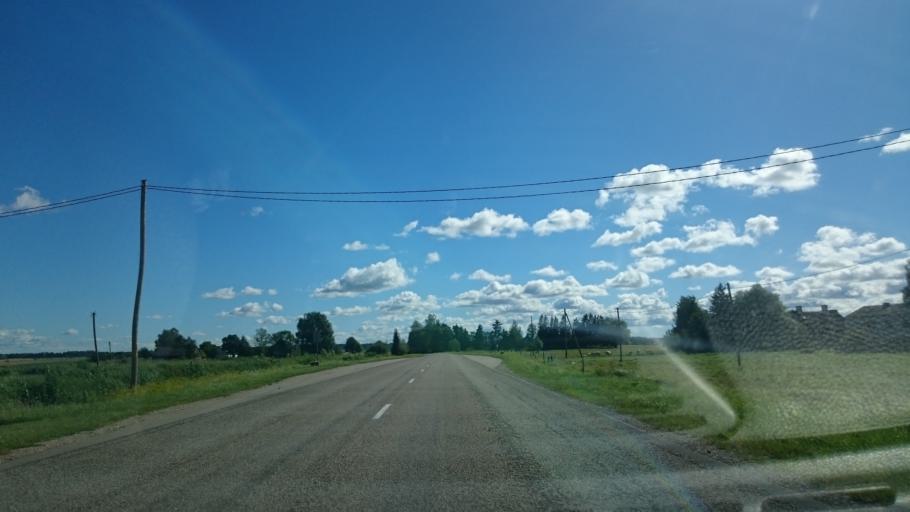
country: LV
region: Aizpute
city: Aizpute
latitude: 56.7633
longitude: 21.6188
